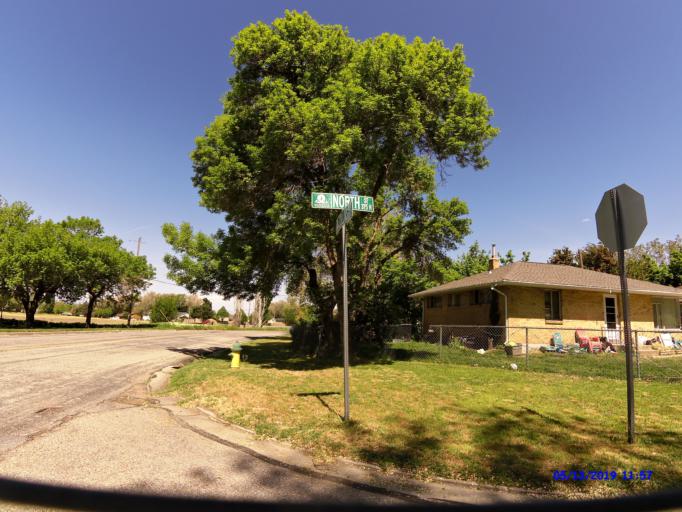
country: US
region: Utah
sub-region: Weber County
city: Harrisville
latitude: 41.2657
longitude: -111.9523
